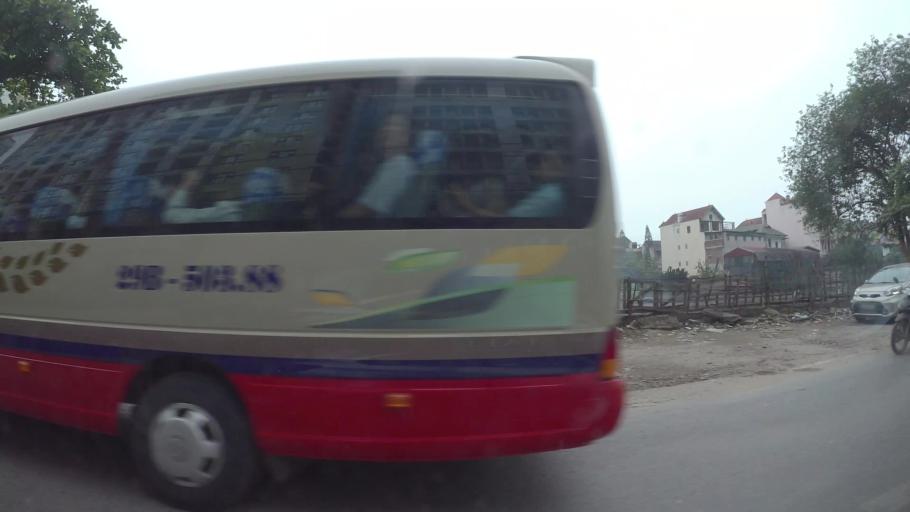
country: VN
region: Ha Noi
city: Tay Ho
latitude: 21.0654
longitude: 105.8274
